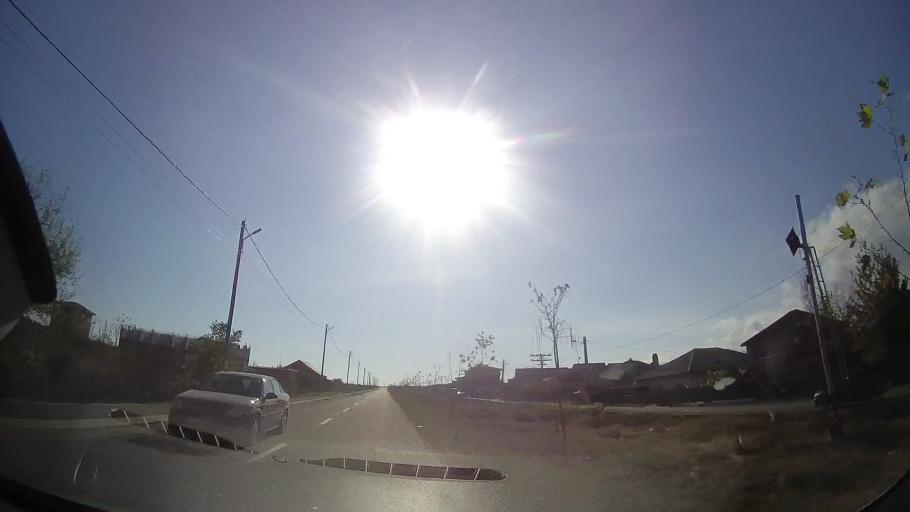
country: RO
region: Constanta
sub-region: Comuna Costinesti
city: Schitu
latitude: 43.9400
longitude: 28.6317
